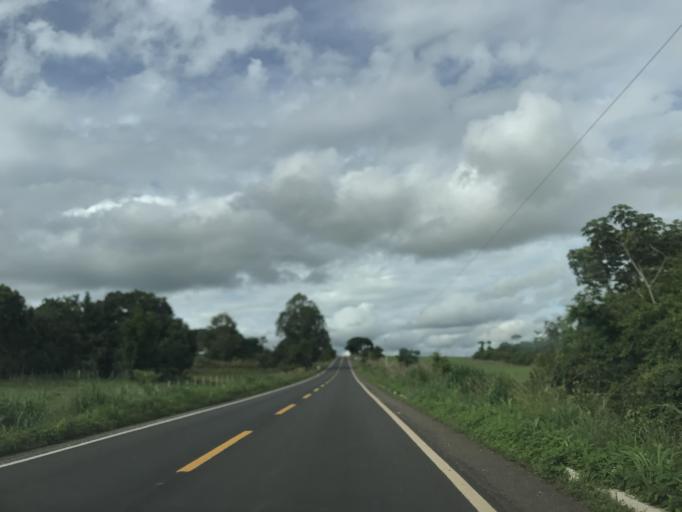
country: BR
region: Goias
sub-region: Piracanjuba
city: Piracanjuba
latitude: -17.1941
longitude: -48.6974
